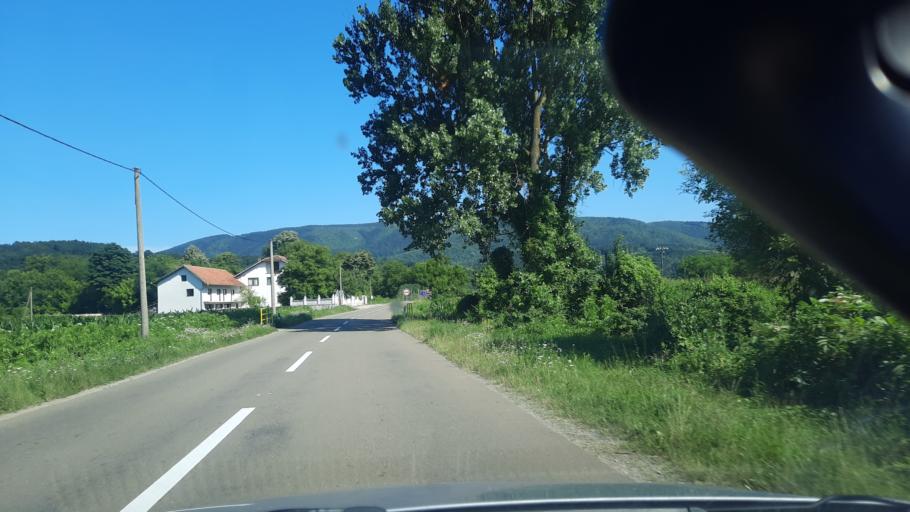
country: RS
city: Turija
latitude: 44.5282
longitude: 21.6326
